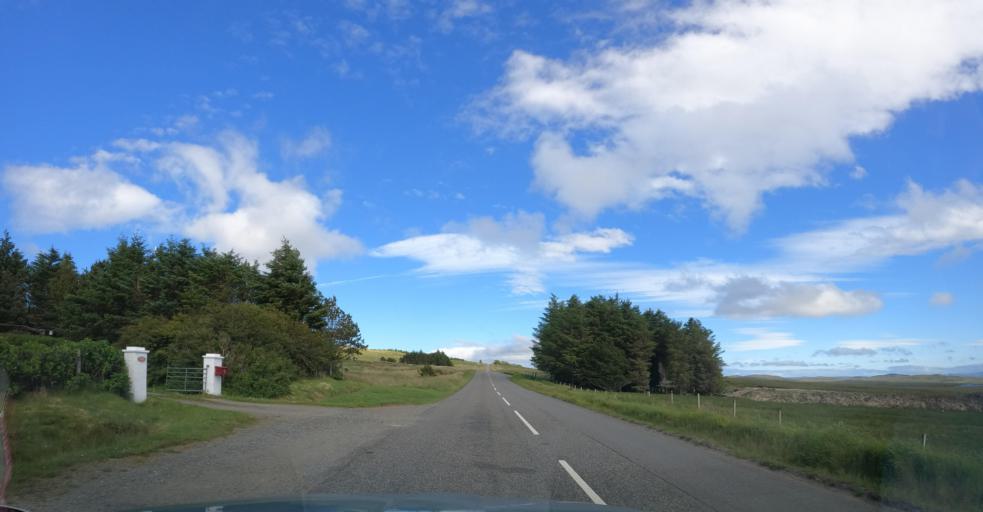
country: GB
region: Scotland
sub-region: Eilean Siar
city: Stornoway
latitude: 58.1737
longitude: -6.6008
